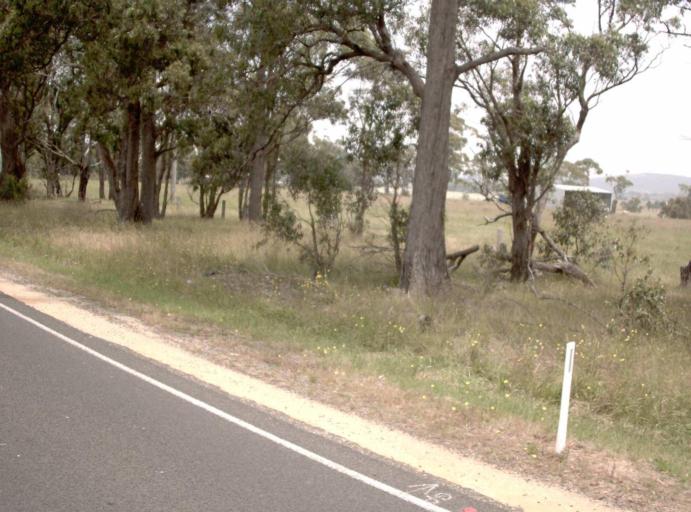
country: AU
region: Victoria
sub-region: Latrobe
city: Traralgon
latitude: -38.4789
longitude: 146.7158
